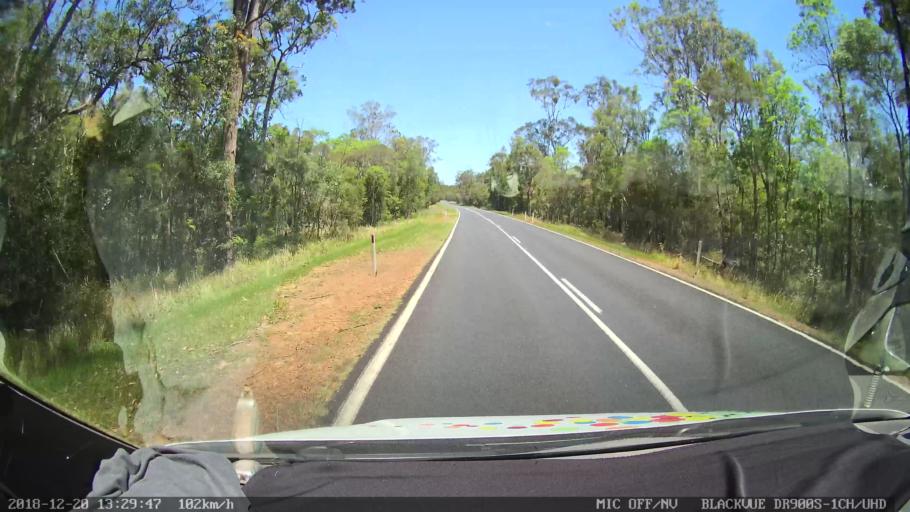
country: AU
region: New South Wales
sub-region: Clarence Valley
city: Gordon
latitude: -29.1941
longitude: 152.9910
